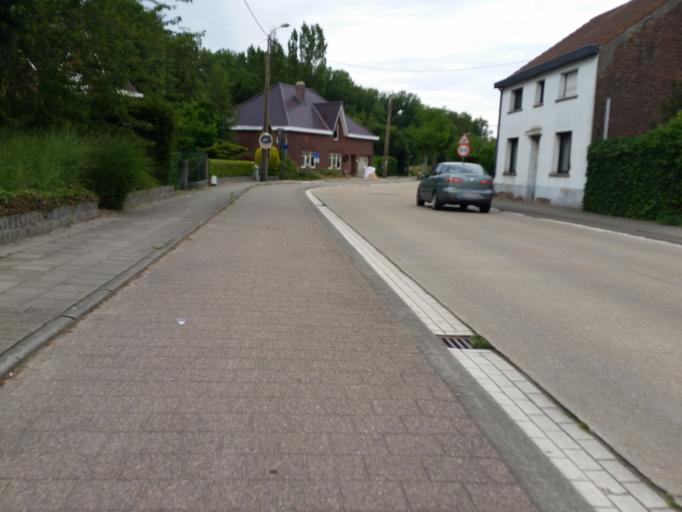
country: BE
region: Flanders
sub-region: Provincie Antwerpen
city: Rumst
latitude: 51.0361
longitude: 4.4243
